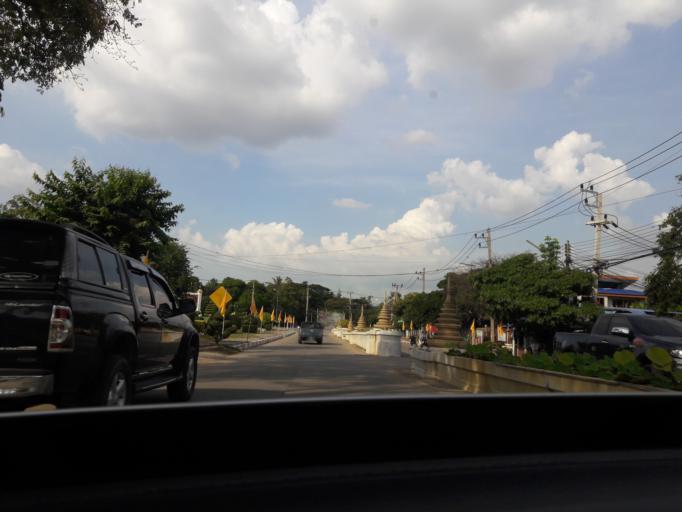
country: TH
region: Sing Buri
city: Sing Buri
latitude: 14.8536
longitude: 100.3887
